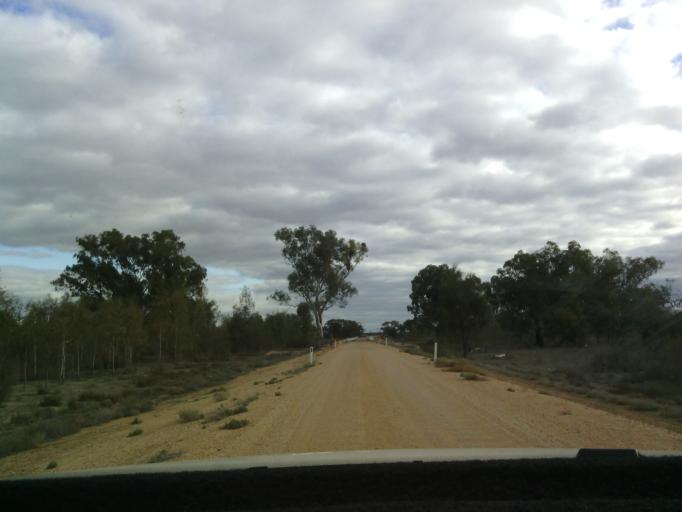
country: AU
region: South Australia
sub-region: Renmark Paringa
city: Renmark
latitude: -34.1673
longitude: 141.1857
